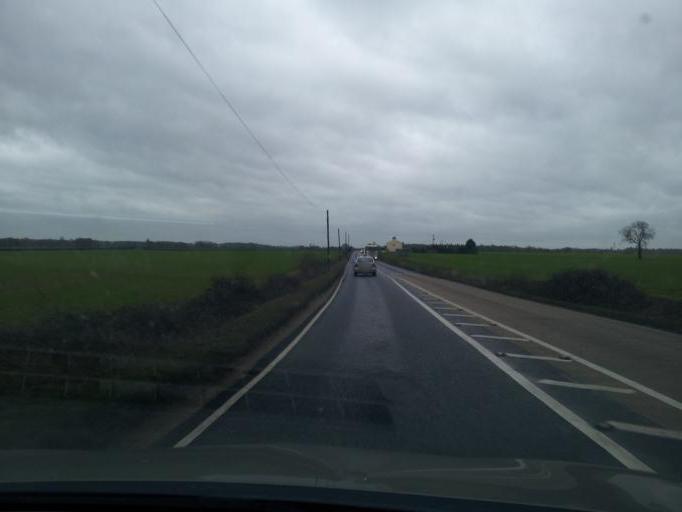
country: GB
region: England
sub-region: Suffolk
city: Thurston
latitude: 52.2819
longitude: 0.8057
